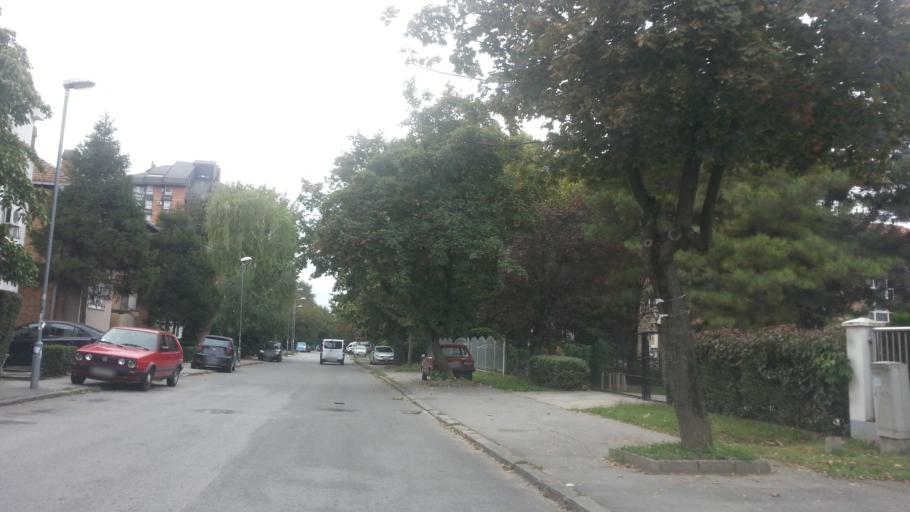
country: RS
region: Central Serbia
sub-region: Belgrade
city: Zemun
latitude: 44.8585
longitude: 20.3665
